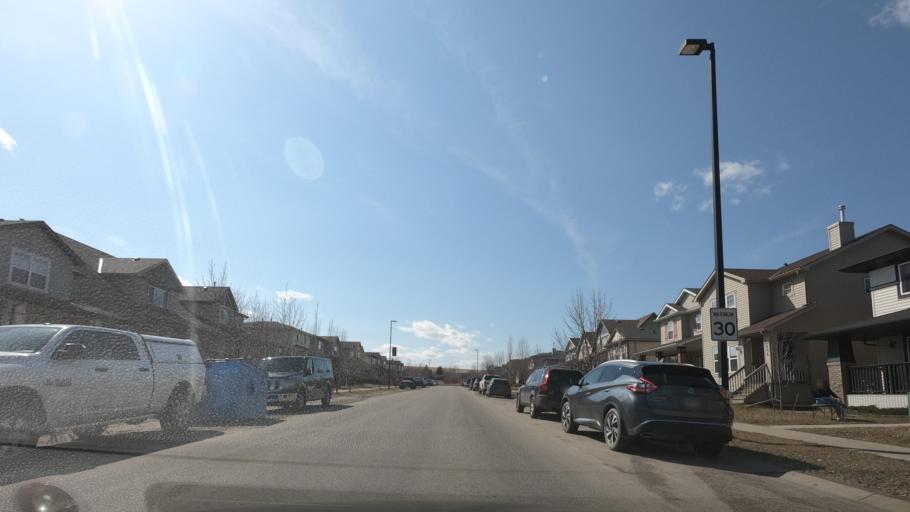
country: CA
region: Alberta
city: Airdrie
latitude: 51.2882
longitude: -114.0455
